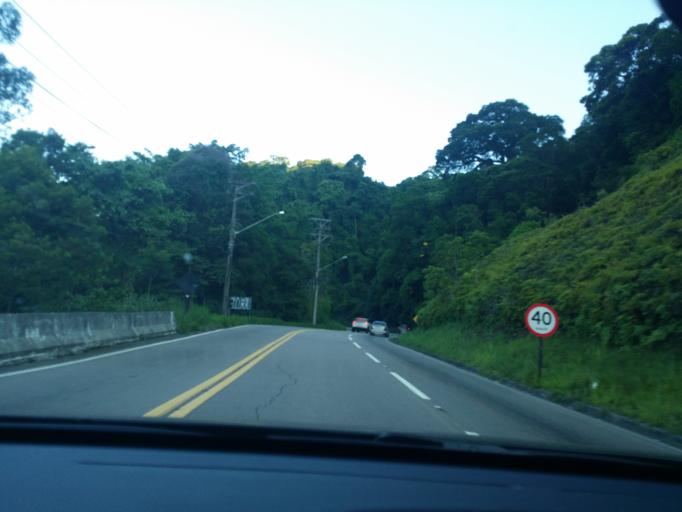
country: BR
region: Sao Paulo
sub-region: Sao Sebastiao
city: Sao Sebastiao
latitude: -23.7814
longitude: -45.6045
